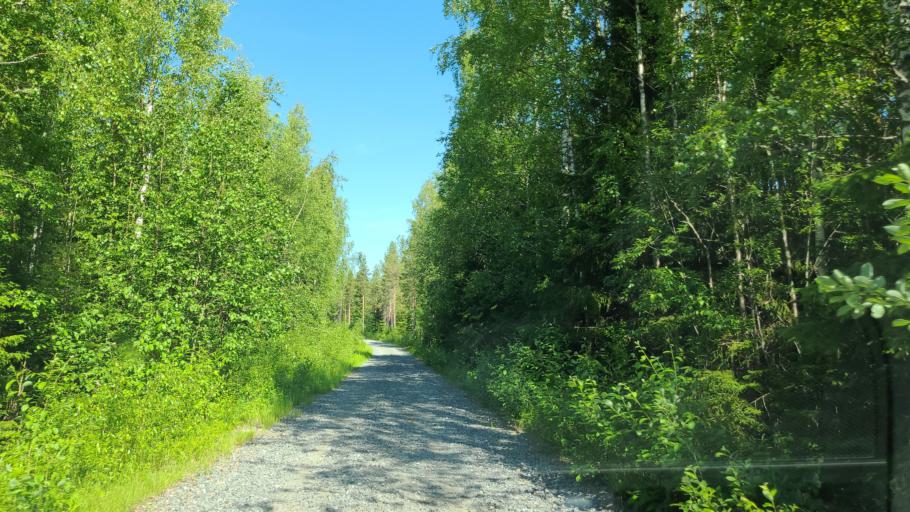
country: SE
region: Vaesterbotten
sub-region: Robertsfors Kommun
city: Robertsfors
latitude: 64.0939
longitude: 20.8352
